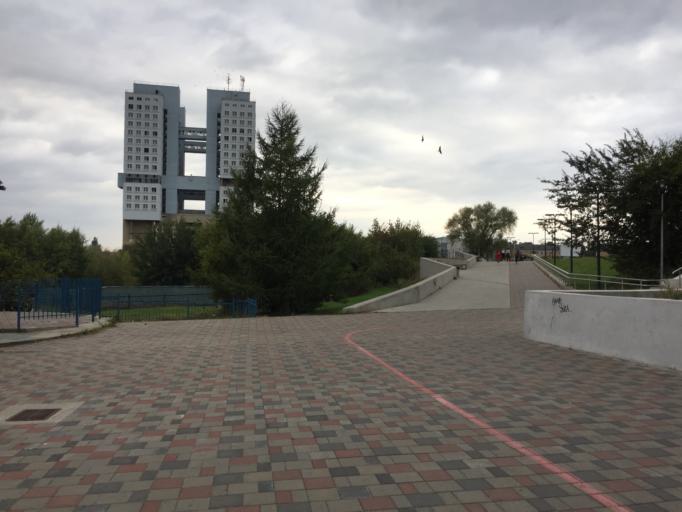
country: RU
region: Kaliningrad
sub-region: Gorod Kaliningrad
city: Kaliningrad
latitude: 54.7094
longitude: 20.5166
